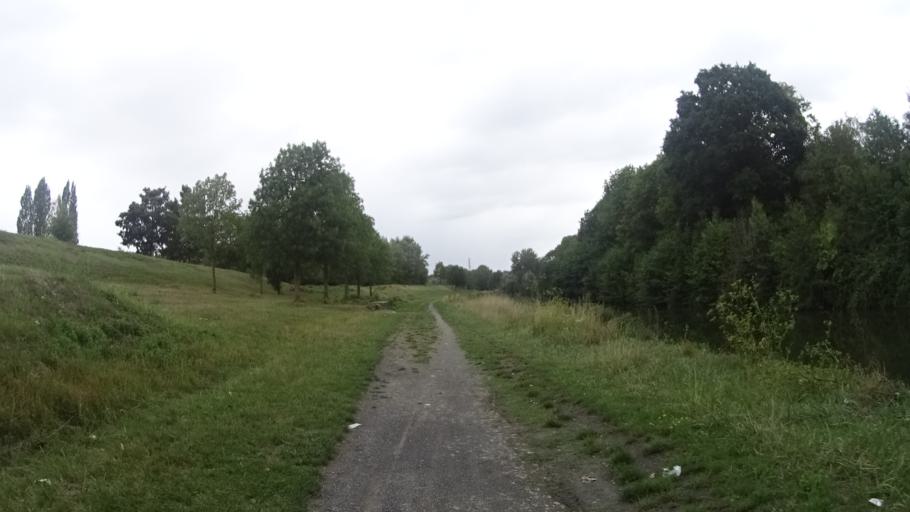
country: FR
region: Nord-Pas-de-Calais
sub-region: Departement du Nord
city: Hautmont
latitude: 50.2541
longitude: 3.9209
